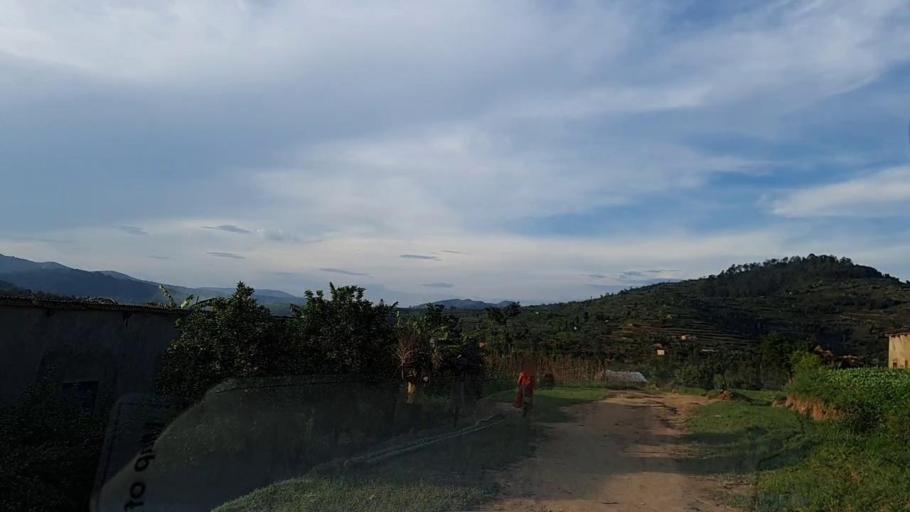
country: RW
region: Southern Province
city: Gikongoro
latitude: -2.4023
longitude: 29.5555
